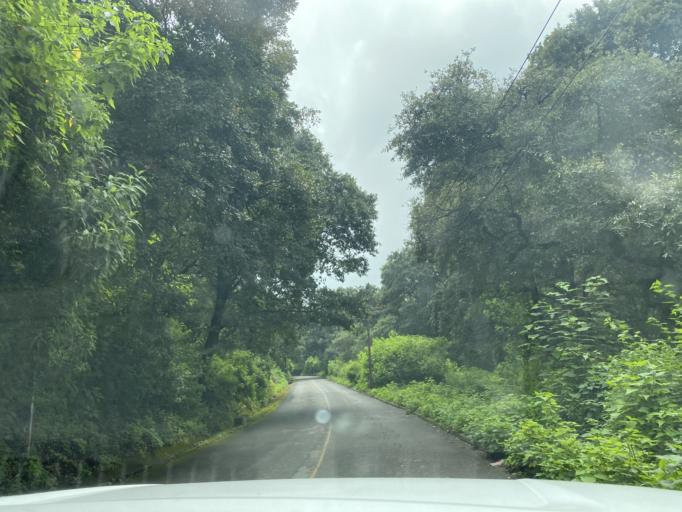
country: MX
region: Morelos
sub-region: Yecapixtla
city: Achichipico
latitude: 18.9397
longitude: -98.8223
